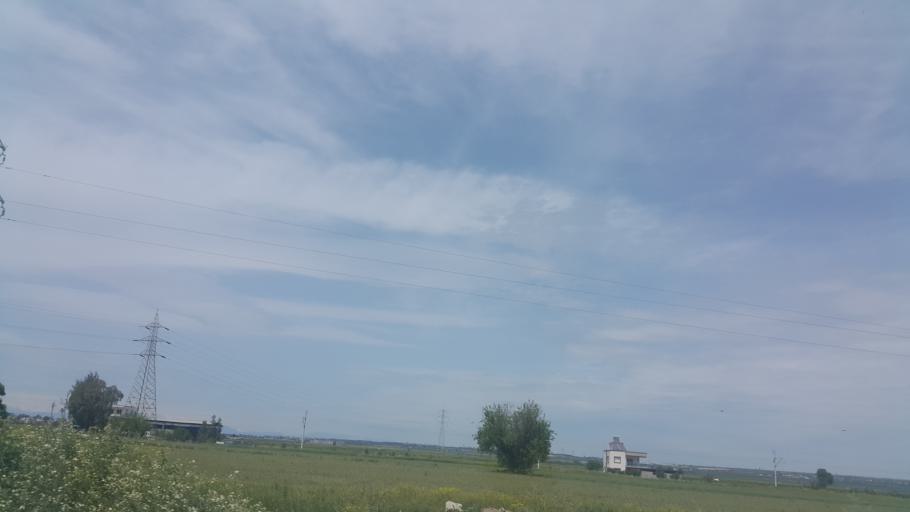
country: TR
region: Adana
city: Yuregir
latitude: 36.9794
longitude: 35.4569
